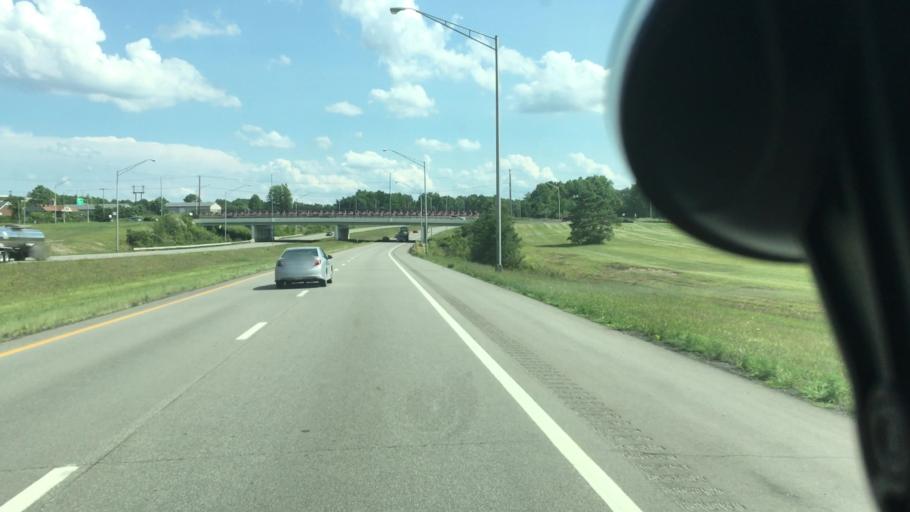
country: US
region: Ohio
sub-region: Mahoning County
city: Austintown
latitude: 41.1019
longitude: -80.7538
